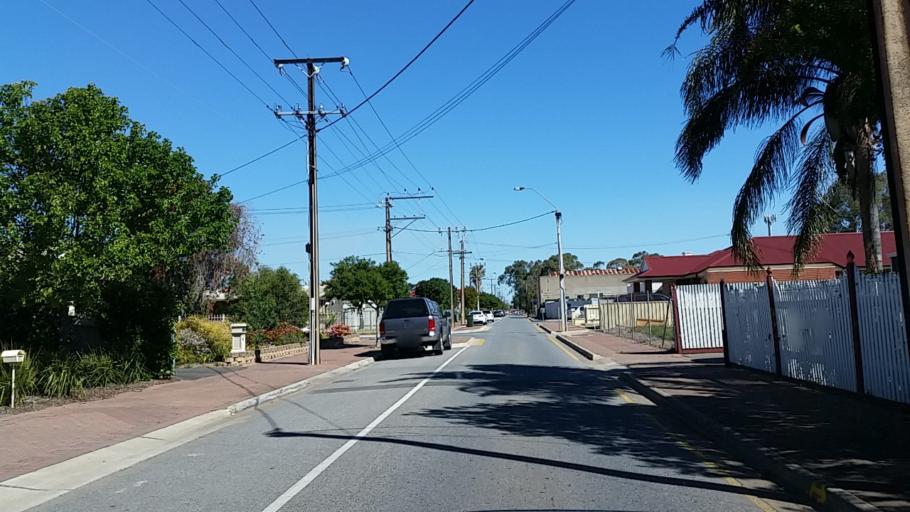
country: AU
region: South Australia
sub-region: Charles Sturt
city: Allenby Gardens
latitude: -34.8936
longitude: 138.5470
